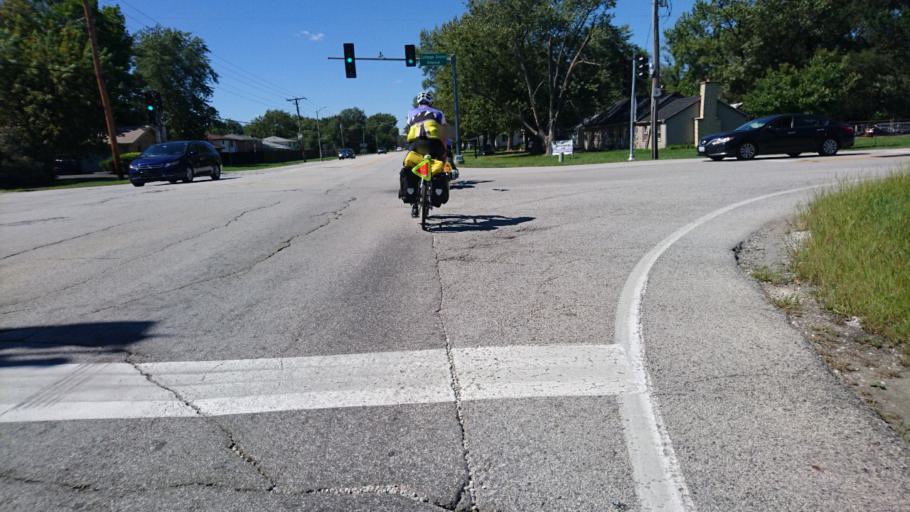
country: US
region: Illinois
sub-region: Cook County
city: Glenwood
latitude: 41.5427
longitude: -87.5971
